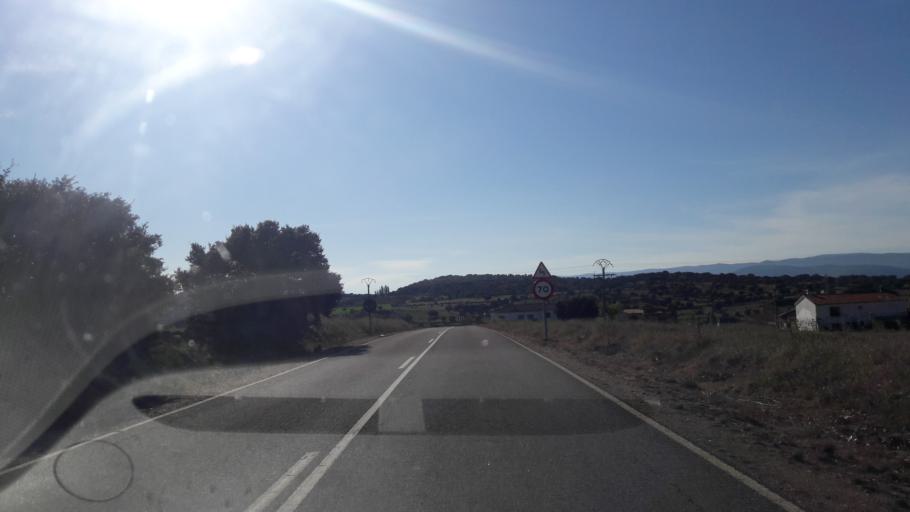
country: ES
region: Castille and Leon
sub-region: Provincia de Salamanca
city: Puente del Congosto
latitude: 40.5239
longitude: -5.5010
